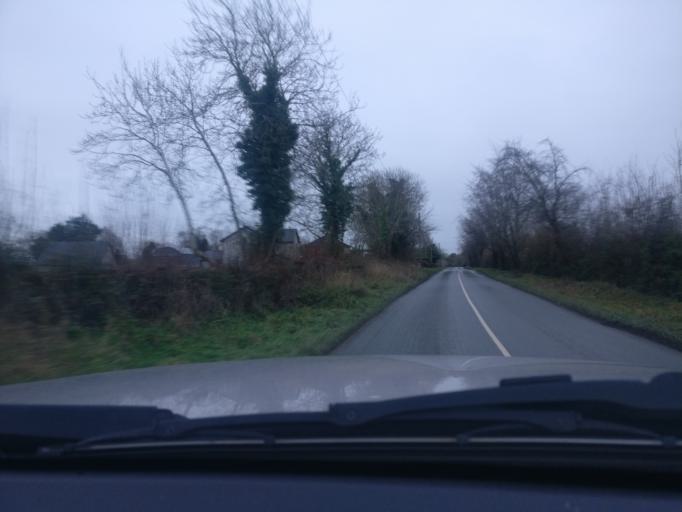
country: IE
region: Leinster
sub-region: Kildare
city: Maynooth
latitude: 53.4030
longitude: -6.6008
